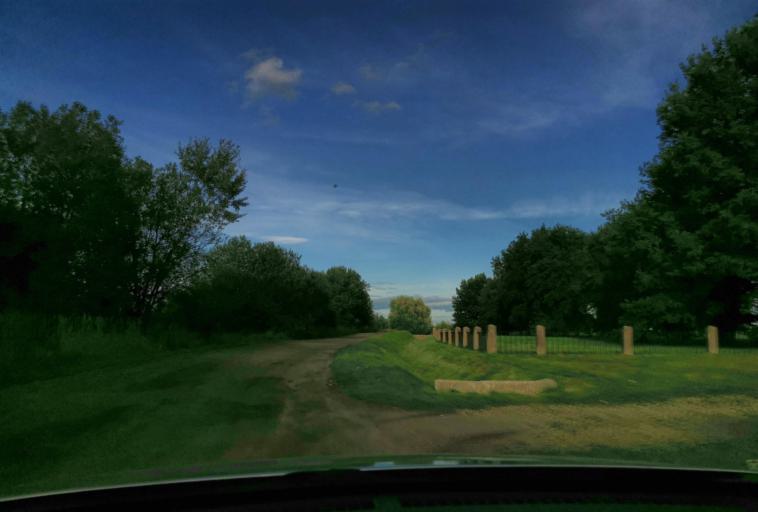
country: RU
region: Kaliningrad
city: Chernyakhovsk
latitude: 54.6230
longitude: 21.8214
